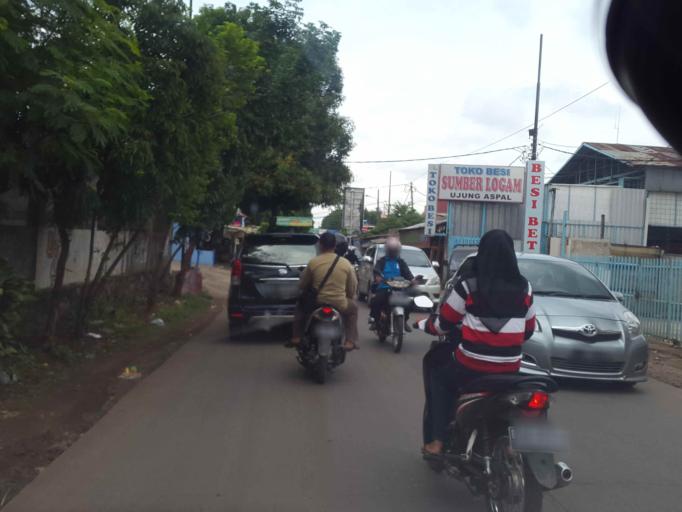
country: ID
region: West Java
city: Cileungsir
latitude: -6.3336
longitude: 106.9237
